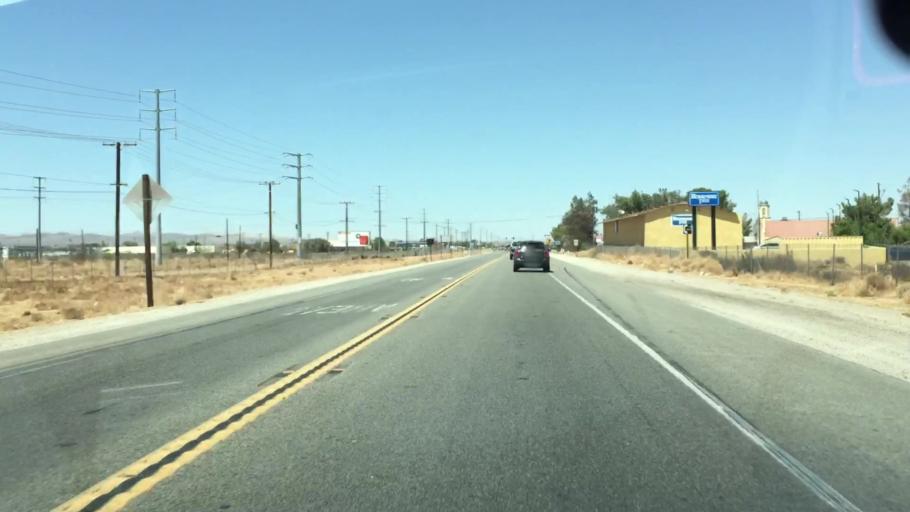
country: US
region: California
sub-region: San Bernardino County
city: Adelanto
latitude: 34.5741
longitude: -117.4103
